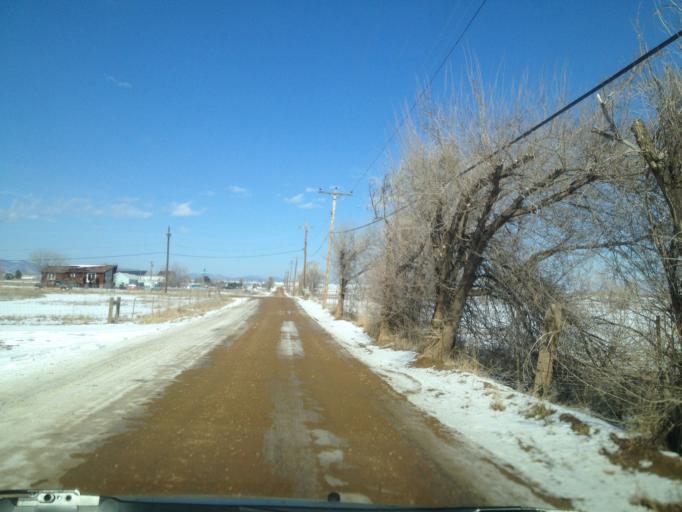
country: US
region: Colorado
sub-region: Boulder County
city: Boulder
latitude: 40.0575
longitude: -105.2633
